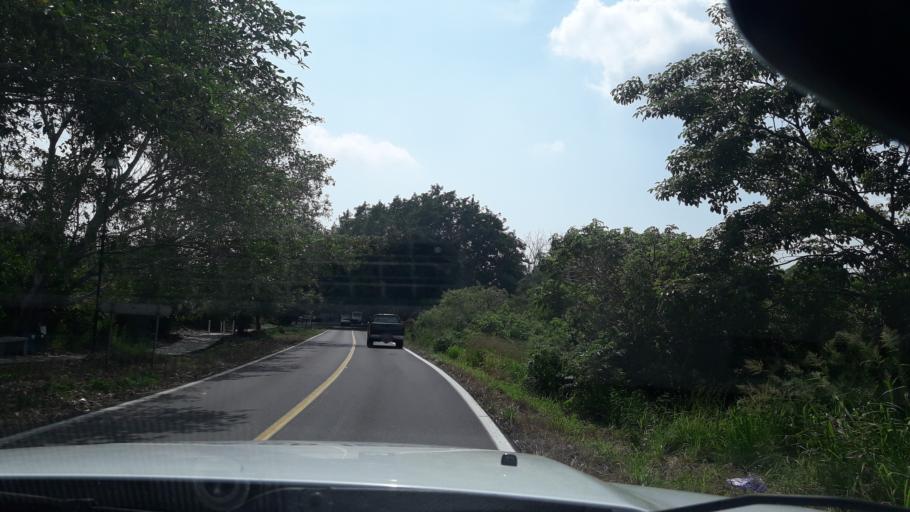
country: MX
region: Colima
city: Suchitlan
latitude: 19.3790
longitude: -103.7155
